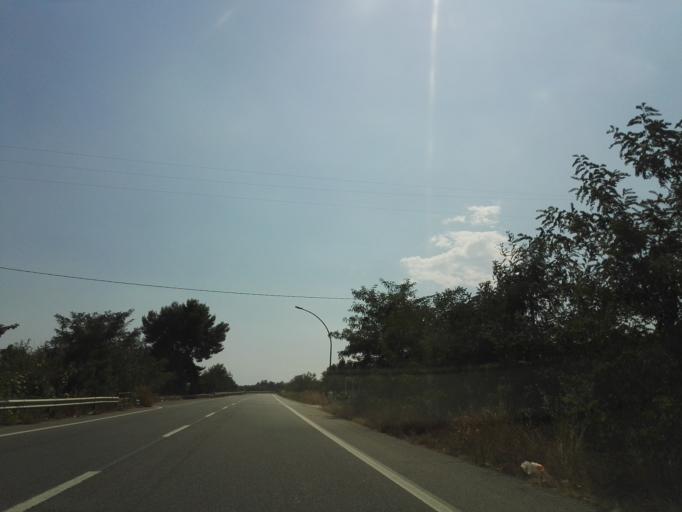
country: IT
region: Calabria
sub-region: Provincia di Reggio Calabria
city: Caulonia Marina
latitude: 38.3633
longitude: 16.4962
